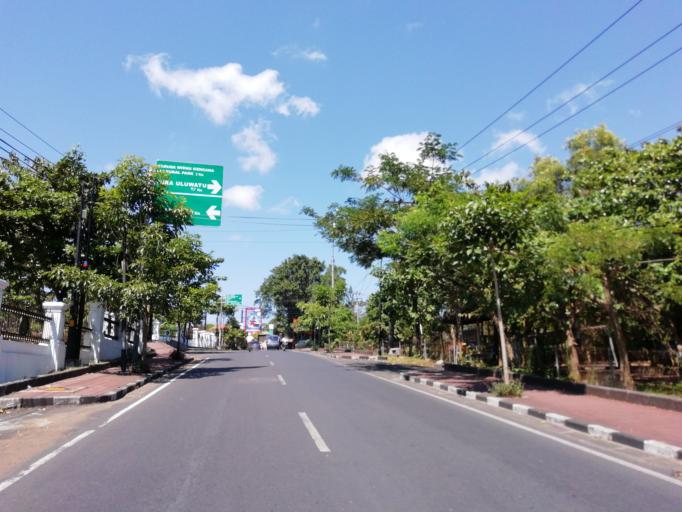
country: ID
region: Bali
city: Jimbaran
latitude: -8.7992
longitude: 115.1710
